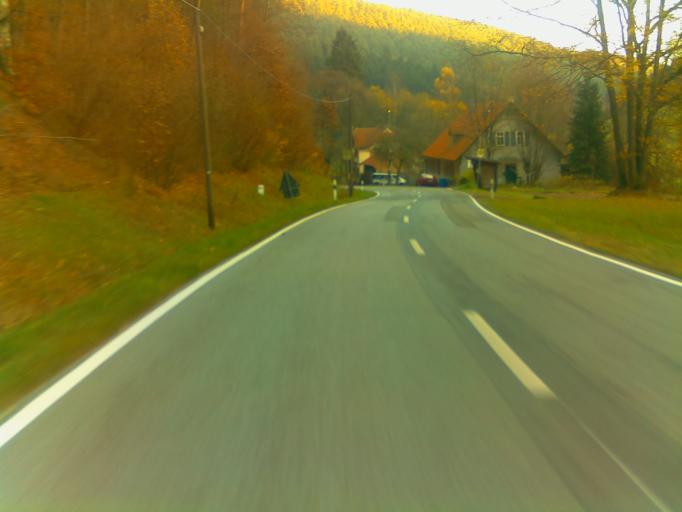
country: DE
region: Hesse
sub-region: Regierungsbezirk Darmstadt
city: Hesseneck
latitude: 49.5778
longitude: 9.0529
